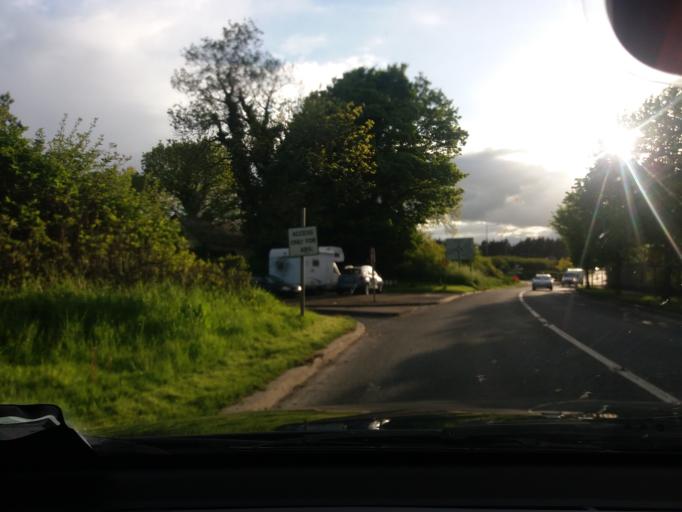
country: IE
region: Leinster
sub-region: South Dublin
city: Rathcoole
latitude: 53.2936
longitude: -6.4788
